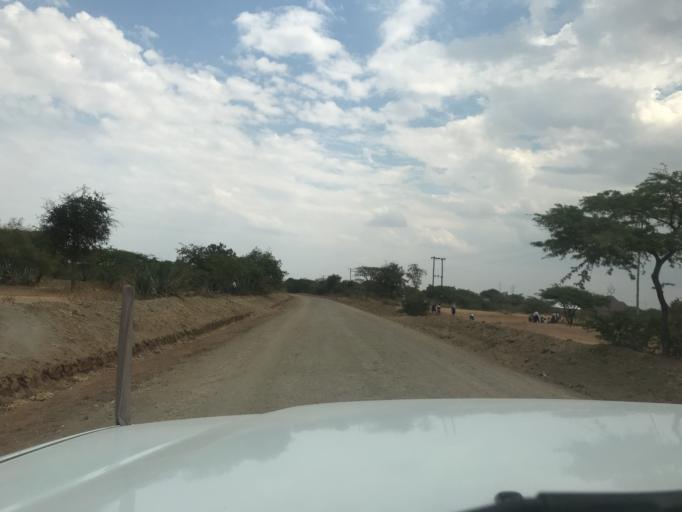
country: TZ
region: Mara
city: Bunda
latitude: -2.0758
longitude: 33.7246
